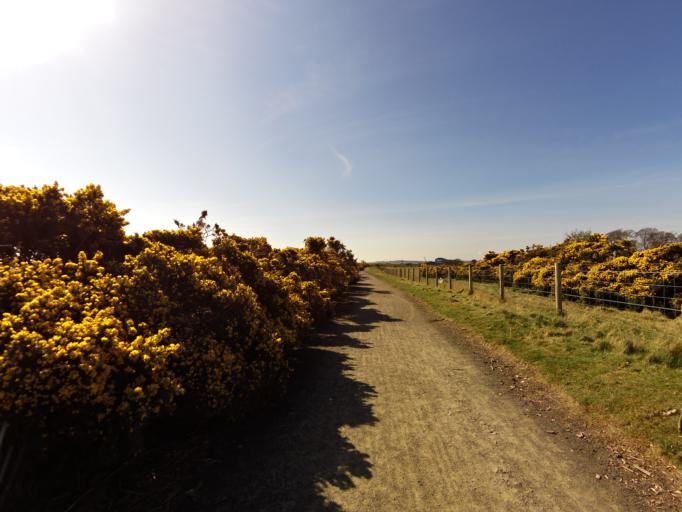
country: GB
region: Scotland
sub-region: Angus
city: Montrose
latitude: 56.7372
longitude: -2.4528
